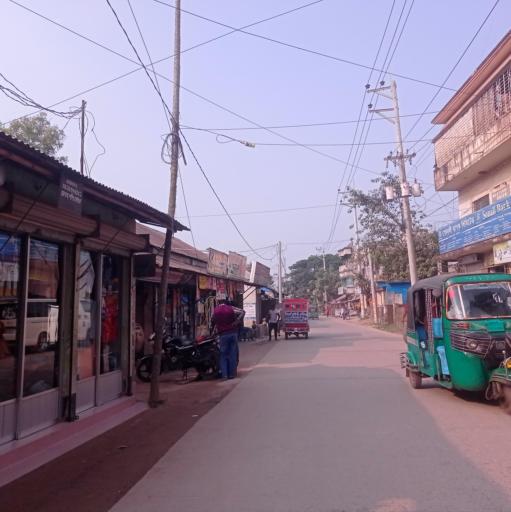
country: BD
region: Dhaka
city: Bhairab Bazar
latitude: 24.1021
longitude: 90.8525
